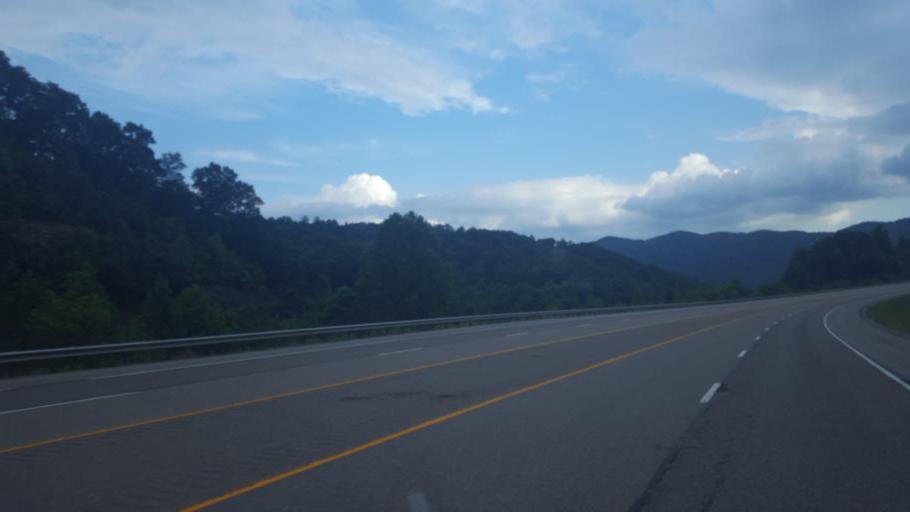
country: US
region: Kentucky
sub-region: Letcher County
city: Jenkins
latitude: 37.2031
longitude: -82.6227
